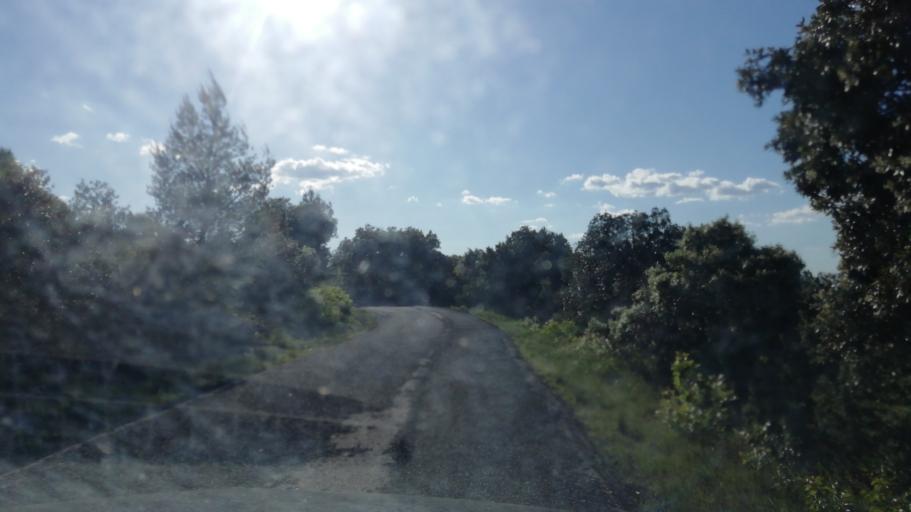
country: FR
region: Languedoc-Roussillon
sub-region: Departement de l'Herault
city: Saint-Mathieu-de-Treviers
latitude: 43.7942
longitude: 3.8103
